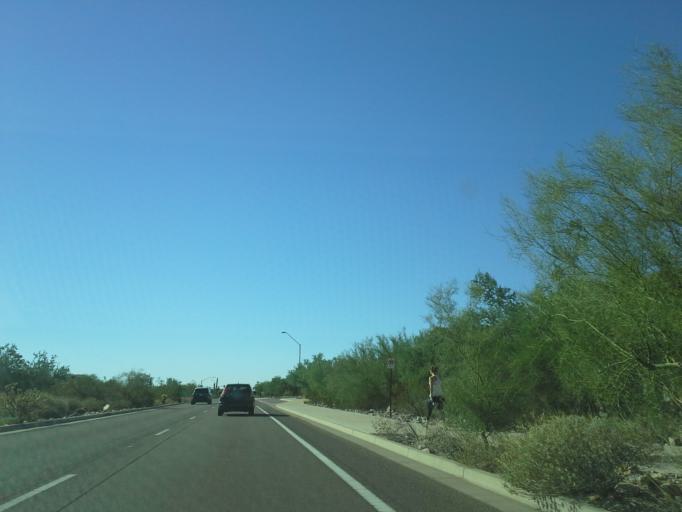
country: US
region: Arizona
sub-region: Maricopa County
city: Scottsdale
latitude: 33.6373
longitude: -111.8610
